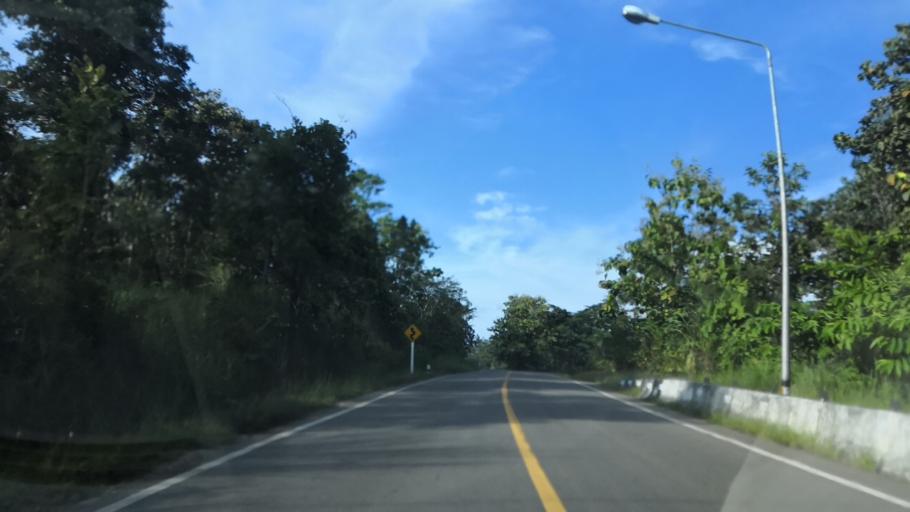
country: TH
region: Mae Hong Son
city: Khun Yuam
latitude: 18.7467
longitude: 97.9270
